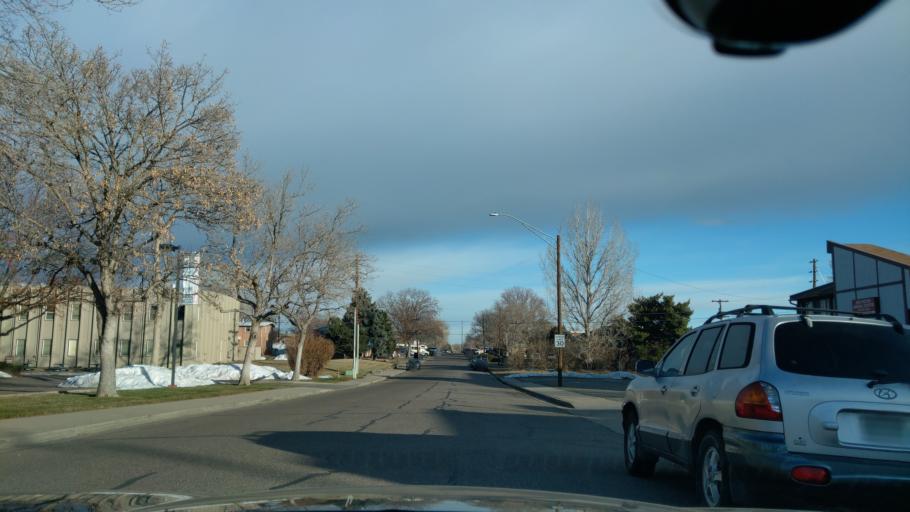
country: US
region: Colorado
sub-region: Jefferson County
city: Lakewood
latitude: 39.7263
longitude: -105.1148
